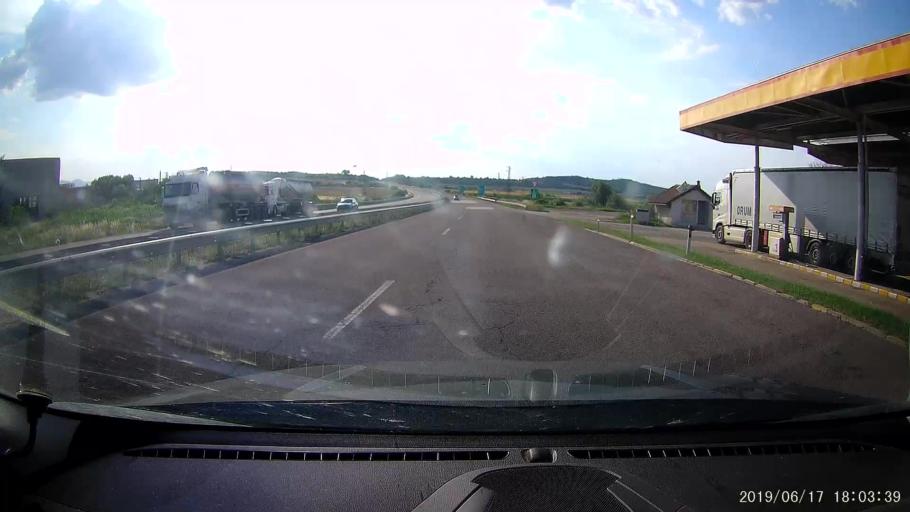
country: BG
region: Khaskovo
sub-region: Obshtina Svilengrad
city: Svilengrad
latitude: 41.7800
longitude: 26.2153
